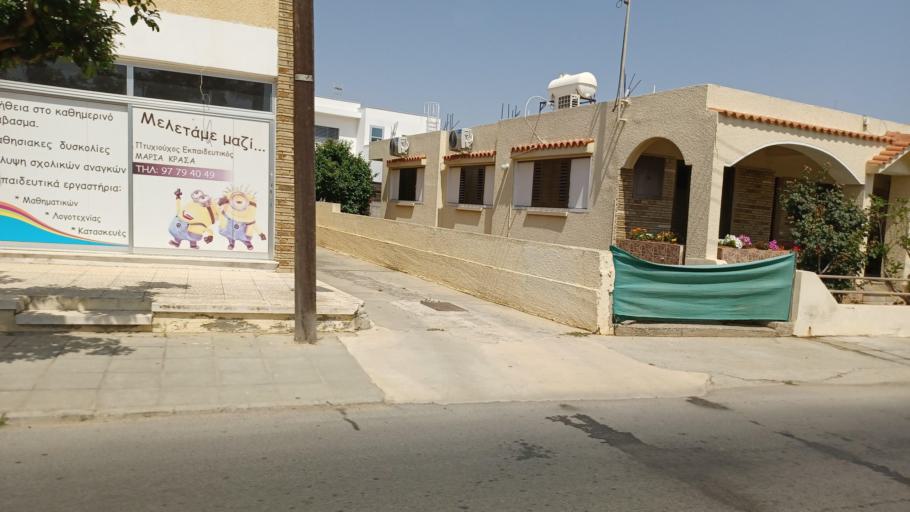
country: CY
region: Ammochostos
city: Paralimni
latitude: 35.0483
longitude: 33.9832
